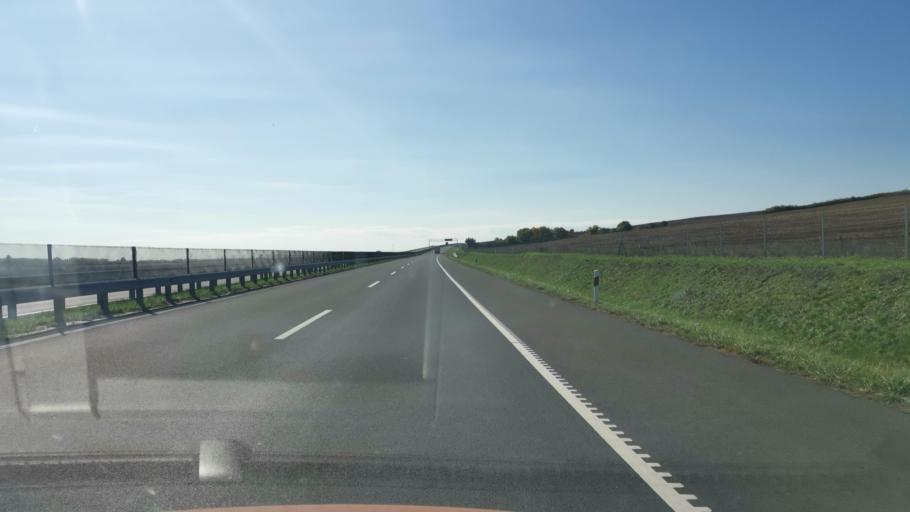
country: HU
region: Borsod-Abauj-Zemplen
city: Halmaj
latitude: 48.2708
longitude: 20.9991
